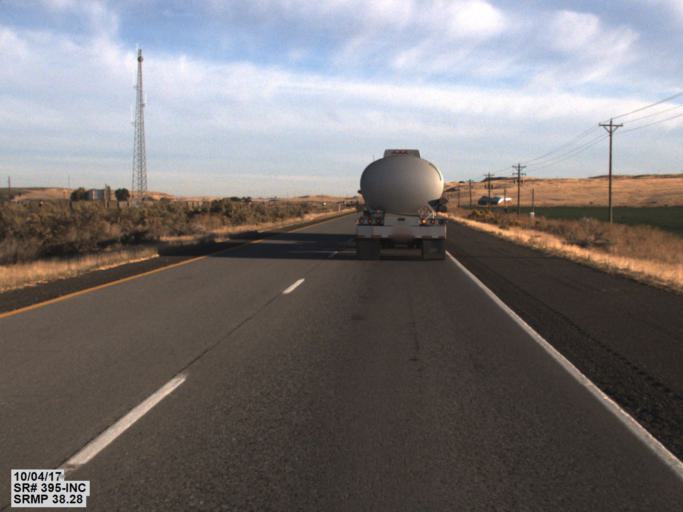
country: US
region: Washington
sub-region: Franklin County
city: Basin City
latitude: 46.4610
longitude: -119.0128
